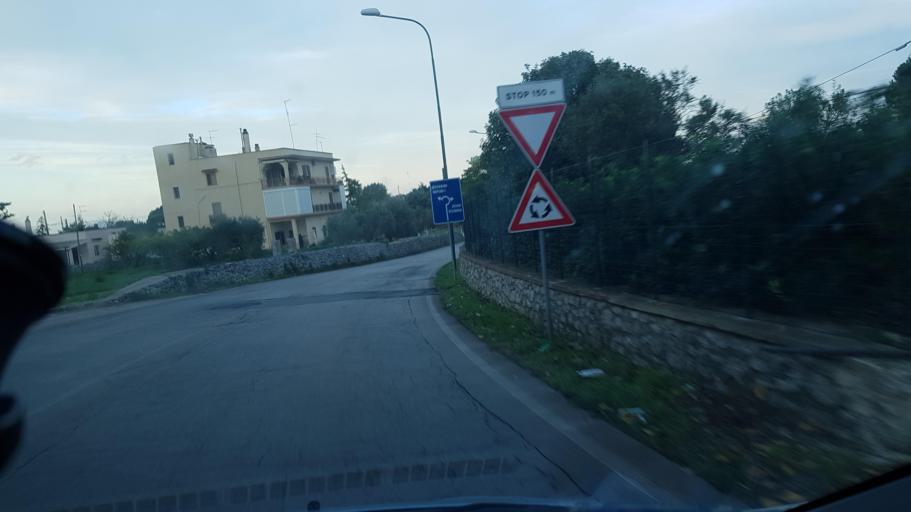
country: IT
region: Apulia
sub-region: Provincia di Brindisi
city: Ceglie Messapica
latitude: 40.6479
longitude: 17.5215
